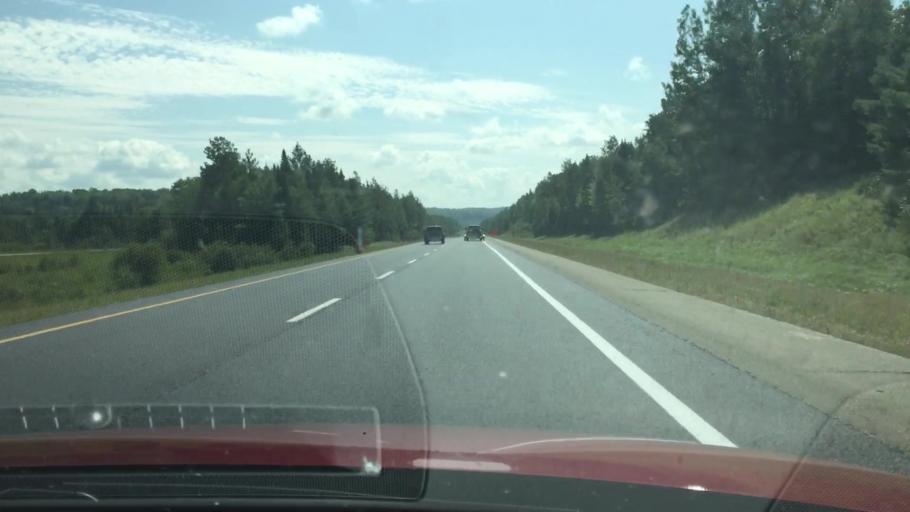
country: US
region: Maine
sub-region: Penobscot County
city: Patten
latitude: 45.8202
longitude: -68.4312
